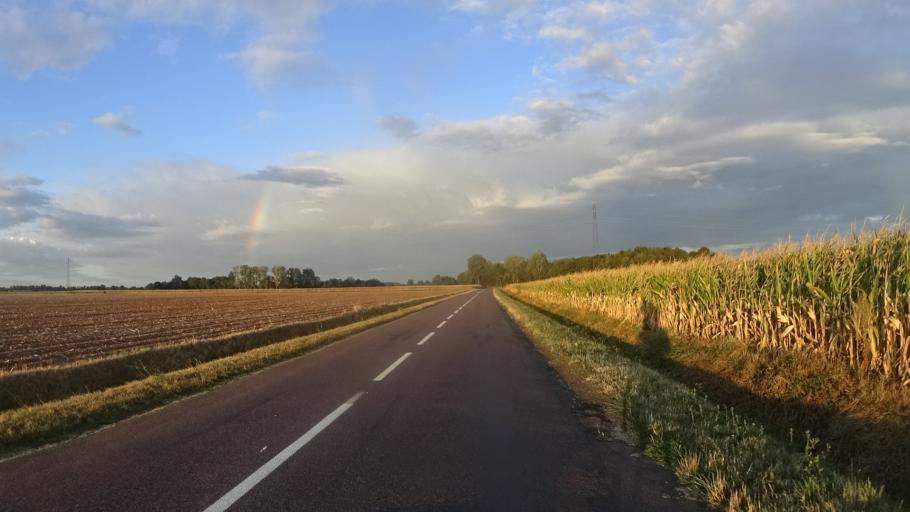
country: FR
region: Bourgogne
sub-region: Departement de la Cote-d'Or
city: Seurre
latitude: 46.9851
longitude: 5.1200
